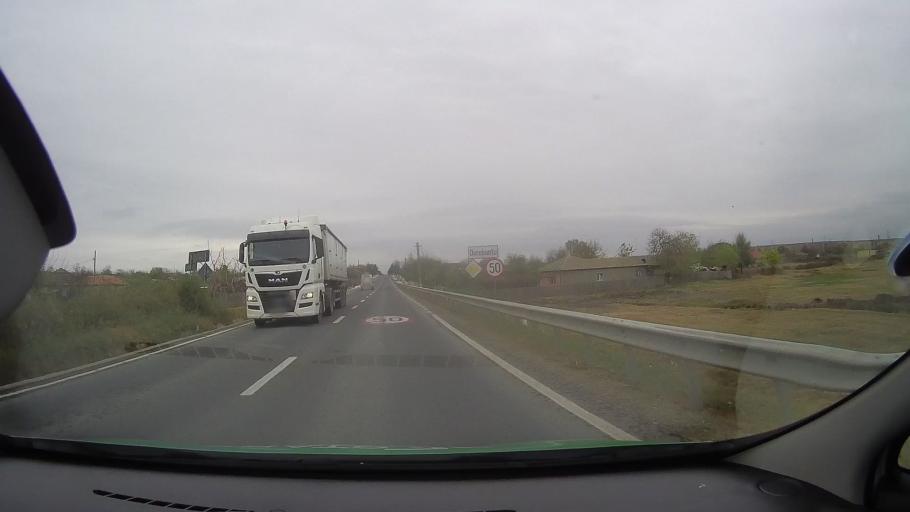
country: RO
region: Constanta
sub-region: Comuna Nicolae Balcescu
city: Dorobantu
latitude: 44.4128
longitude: 28.3202
